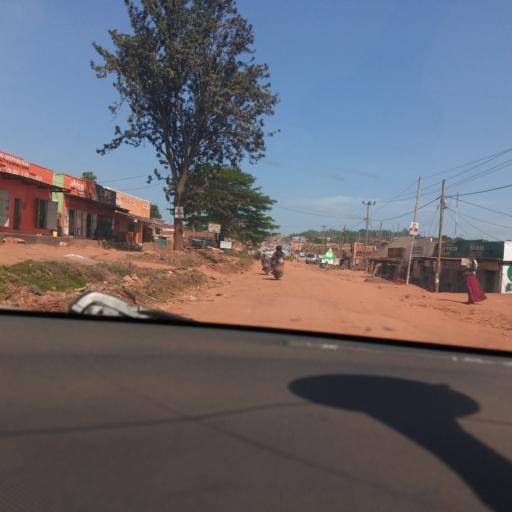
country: UG
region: Central Region
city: Masaka
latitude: -0.3142
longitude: 31.7583
